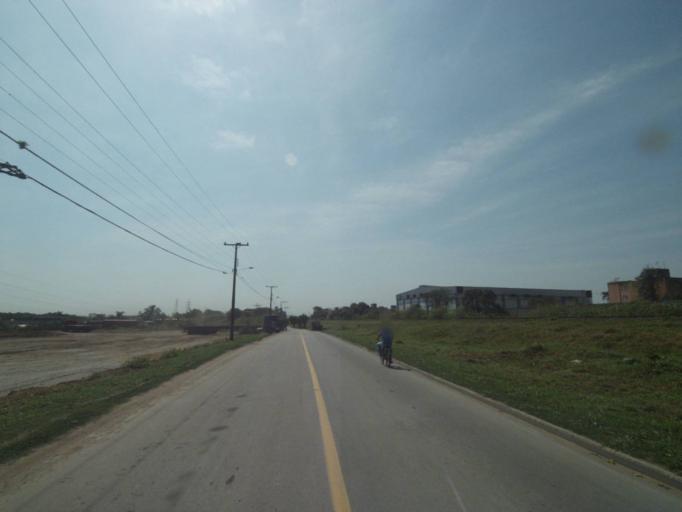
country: BR
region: Parana
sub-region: Paranagua
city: Paranagua
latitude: -25.5487
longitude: -48.5543
